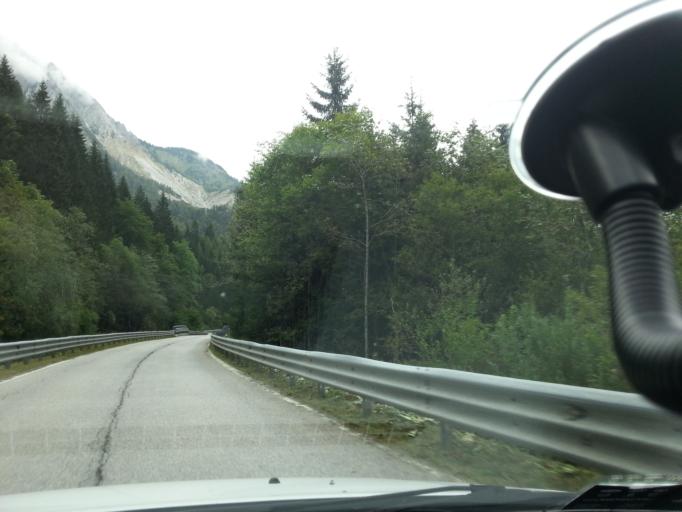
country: IT
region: Friuli Venezia Giulia
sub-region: Provincia di Udine
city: Forni Avoltri
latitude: 46.5745
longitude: 12.7509
